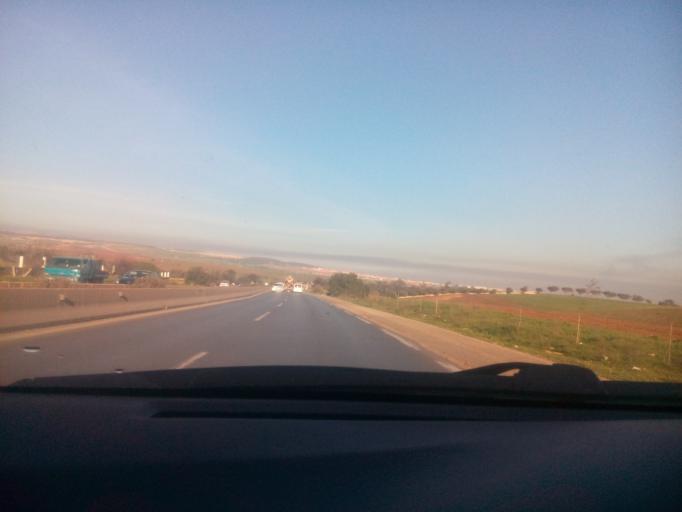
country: DZ
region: Oran
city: Bir el Djir
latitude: 35.7595
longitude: -0.4722
